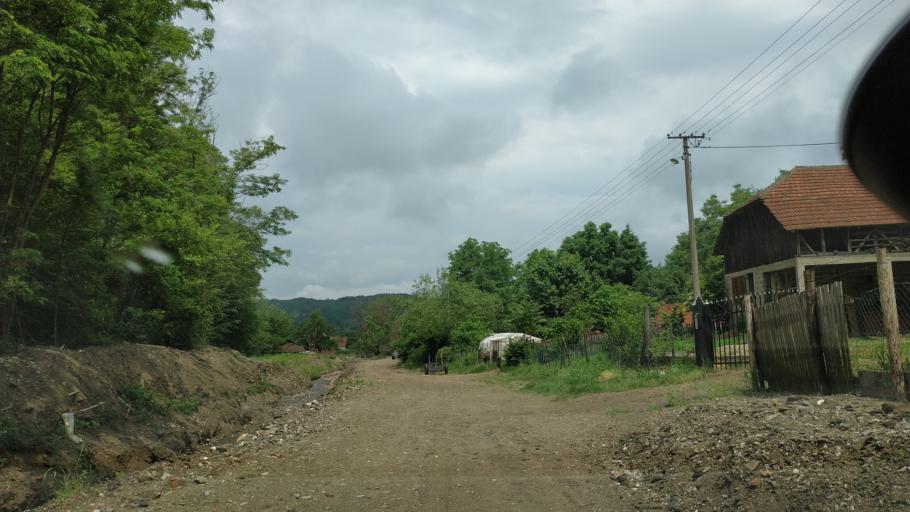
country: RS
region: Central Serbia
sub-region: Nisavski Okrug
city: Aleksinac
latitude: 43.4258
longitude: 21.6534
